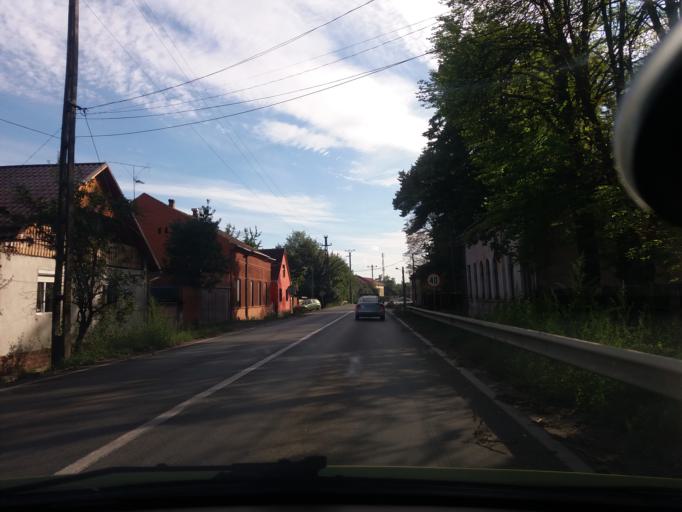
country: RO
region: Arad
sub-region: Oras Lipova
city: Radna
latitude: 46.0959
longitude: 21.6871
